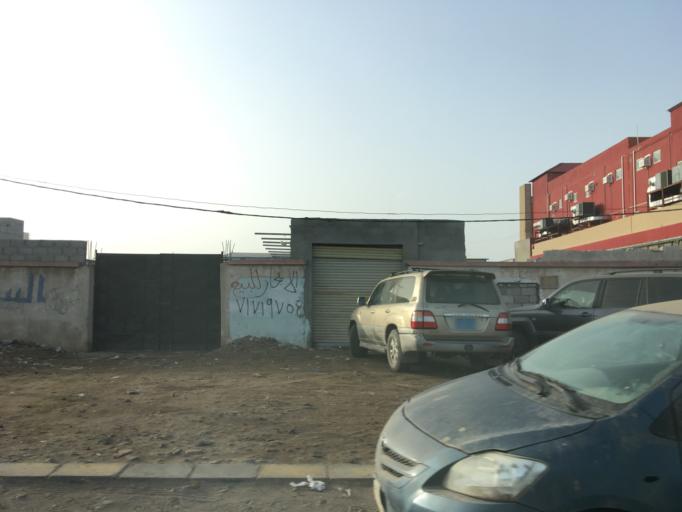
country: YE
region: Aden
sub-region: Ash Shaikh Outhman
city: Ash Shaykh `Uthman
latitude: 12.8589
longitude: 45.0058
